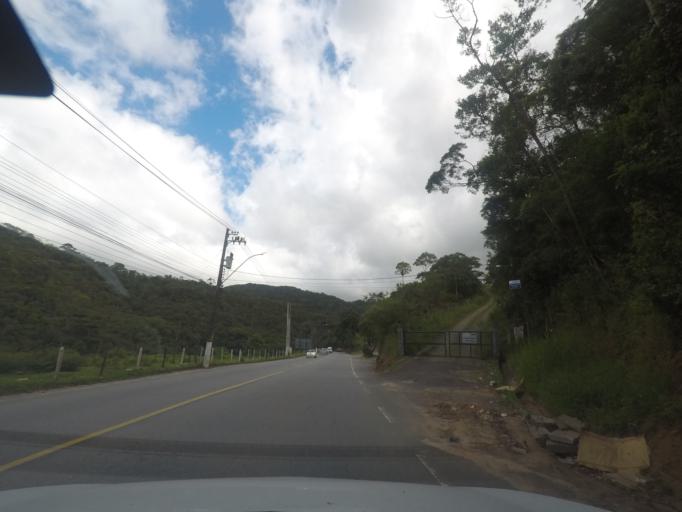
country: BR
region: Rio de Janeiro
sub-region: Teresopolis
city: Teresopolis
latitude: -22.3910
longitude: -42.9571
